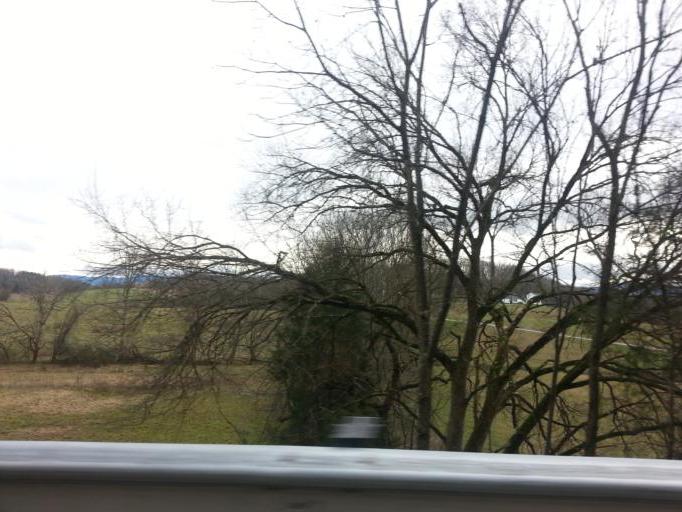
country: US
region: Tennessee
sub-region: Greene County
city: Mosheim
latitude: 36.0801
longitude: -82.9595
